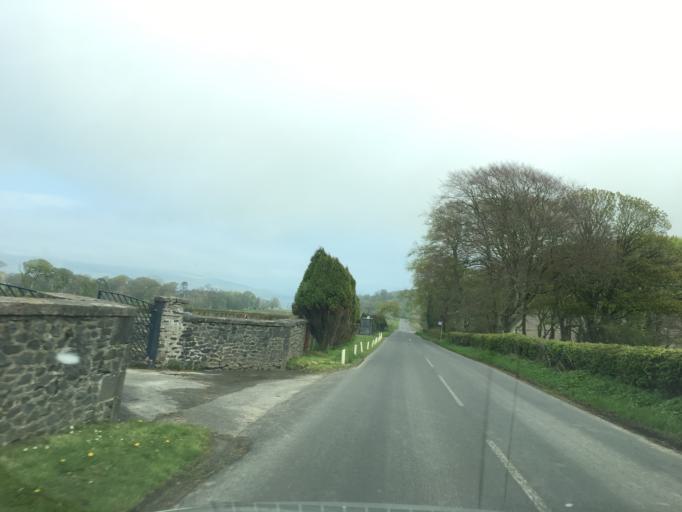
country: GB
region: Scotland
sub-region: Argyll and Bute
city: Port Bannatyne
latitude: 55.8595
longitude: -5.1110
